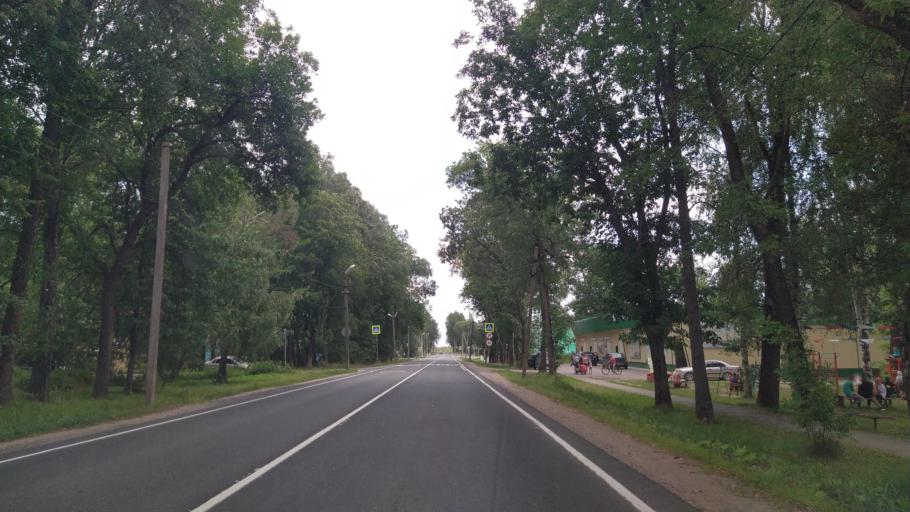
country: RU
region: Pskov
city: Pskov
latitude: 57.7617
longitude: 28.7587
